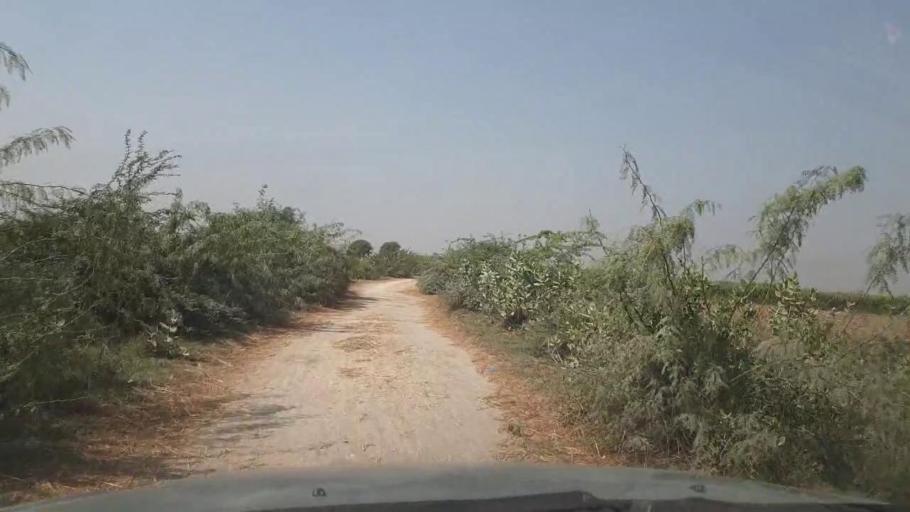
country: PK
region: Sindh
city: Bulri
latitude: 24.8690
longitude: 68.3231
